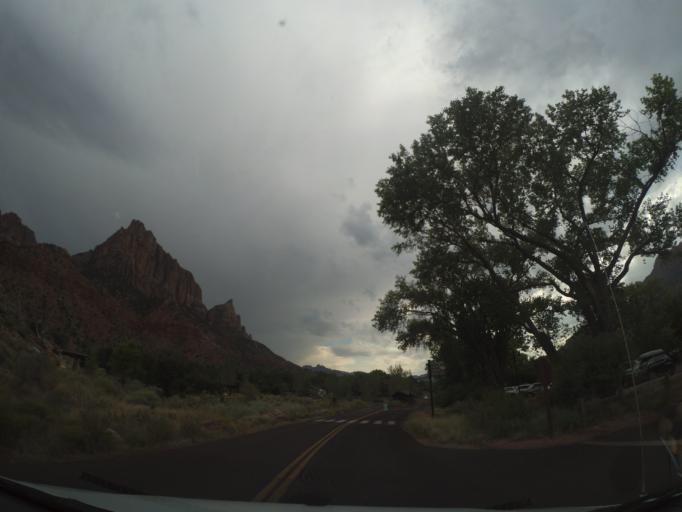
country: US
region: Utah
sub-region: Washington County
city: Hildale
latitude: 37.1992
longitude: -112.9858
